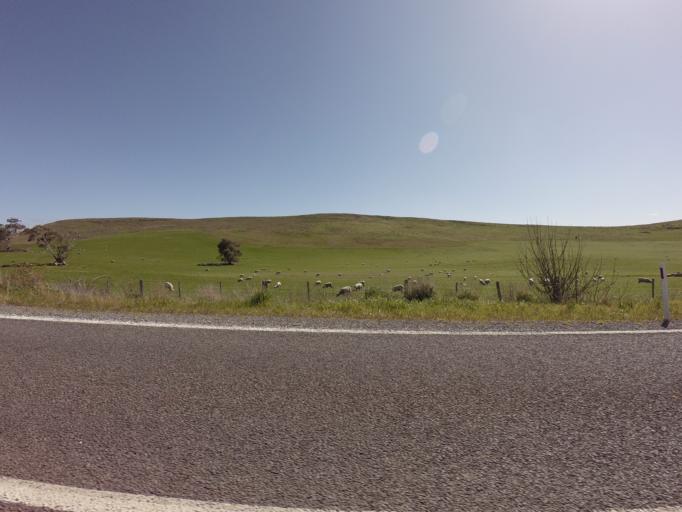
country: AU
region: Tasmania
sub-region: Derwent Valley
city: New Norfolk
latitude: -42.5785
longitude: 146.8818
